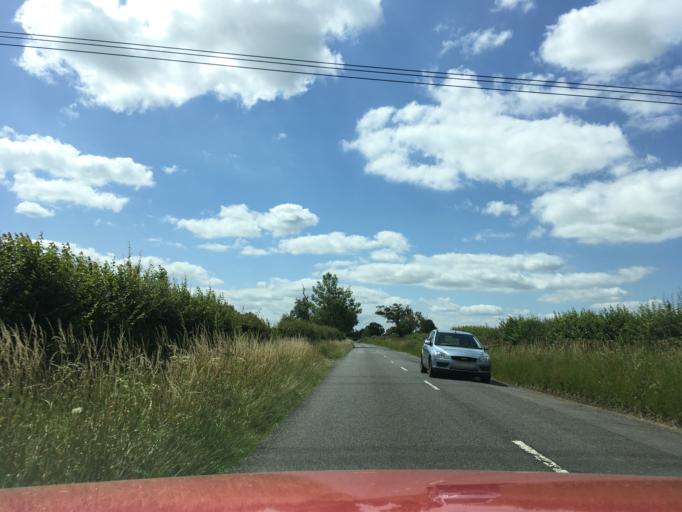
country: GB
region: England
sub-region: Buckinghamshire
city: Winslow
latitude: 51.9252
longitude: -0.8372
